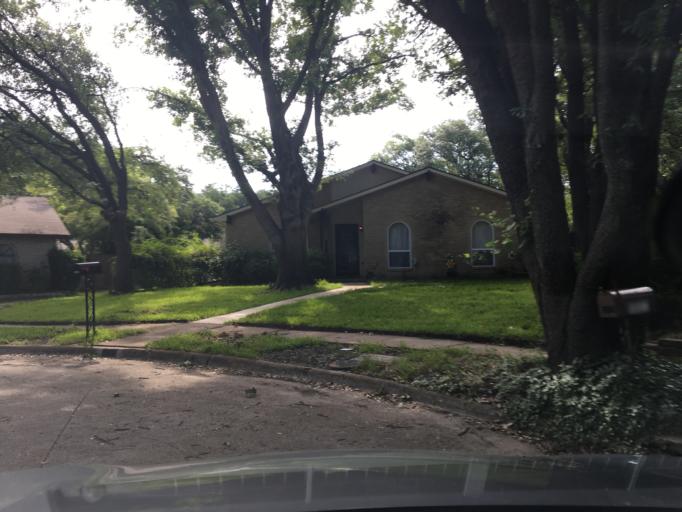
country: US
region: Texas
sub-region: Collin County
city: Plano
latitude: 32.9698
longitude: -96.6790
